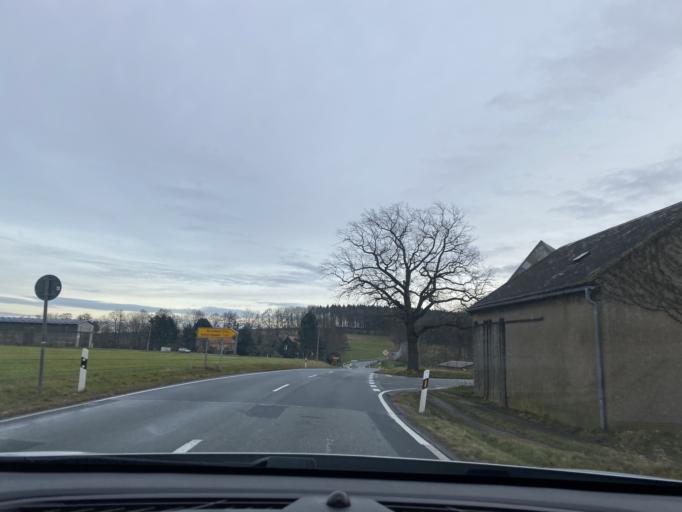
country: DE
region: Saxony
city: Reichenbach
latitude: 51.1175
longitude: 14.8334
